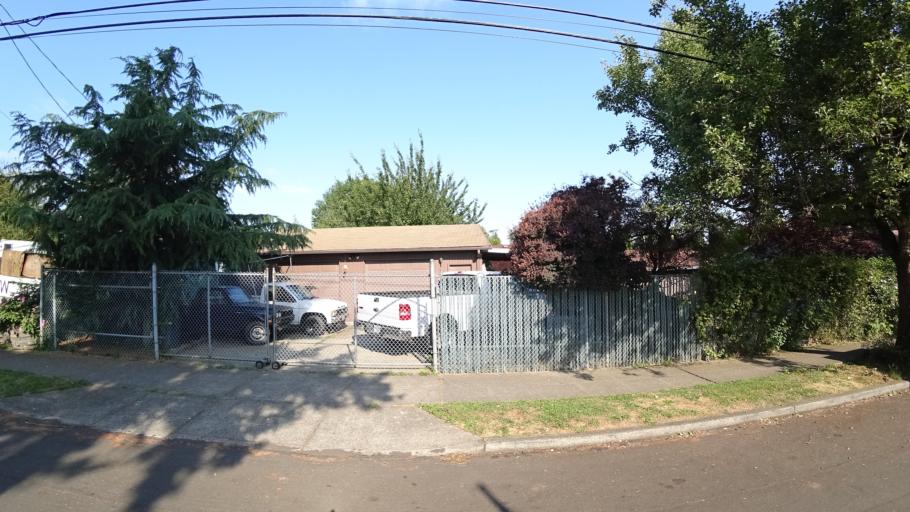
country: US
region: Oregon
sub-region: Washington County
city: West Haven
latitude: 45.5966
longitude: -122.7437
